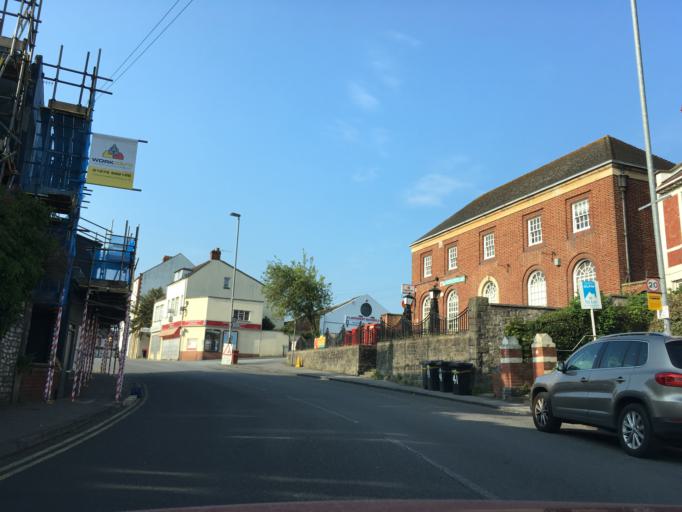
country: GB
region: England
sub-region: Bristol
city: Bristol
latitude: 51.4942
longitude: -2.6185
